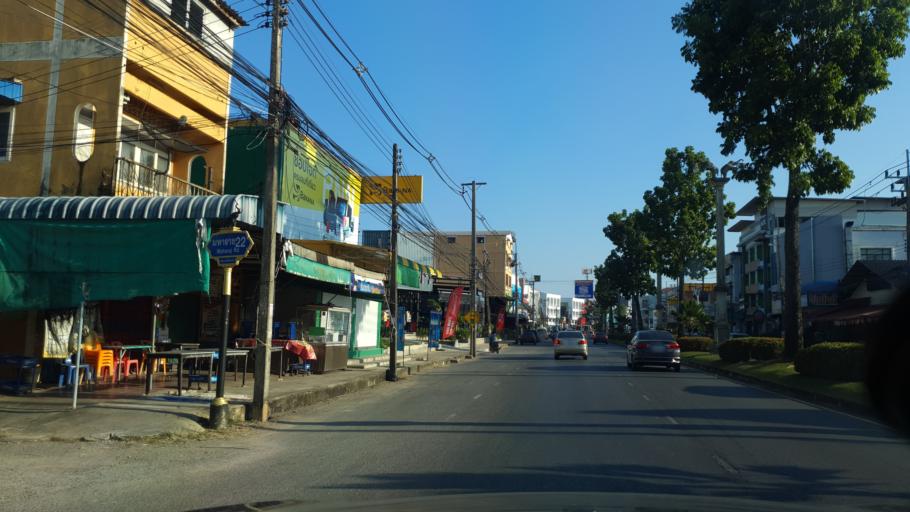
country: TH
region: Krabi
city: Krabi
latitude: 8.0688
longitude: 98.9138
